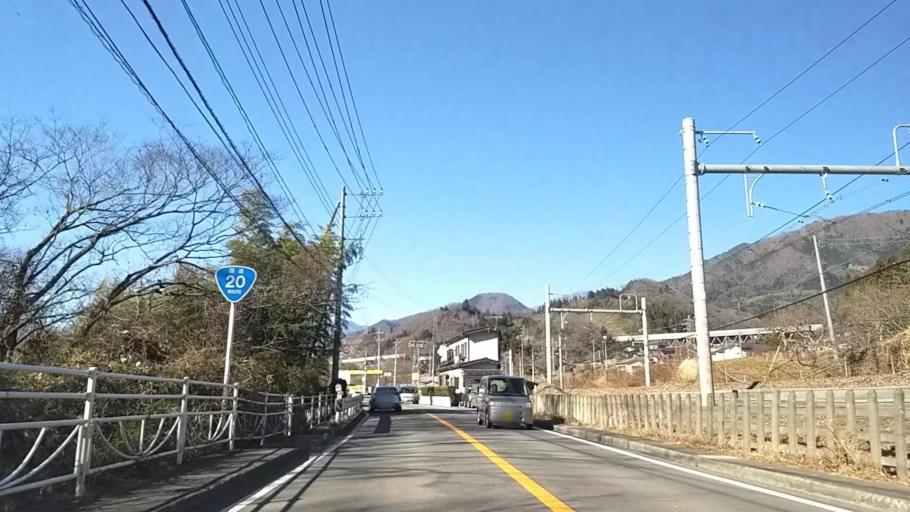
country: JP
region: Yamanashi
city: Otsuki
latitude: 35.6054
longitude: 139.0160
